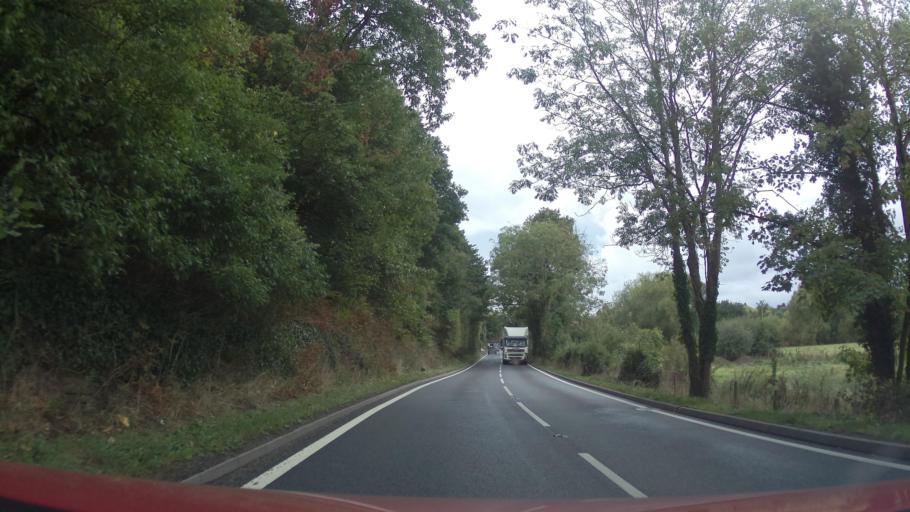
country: GB
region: England
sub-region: Shropshire
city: Bridgnorth
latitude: 52.5484
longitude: -2.4071
